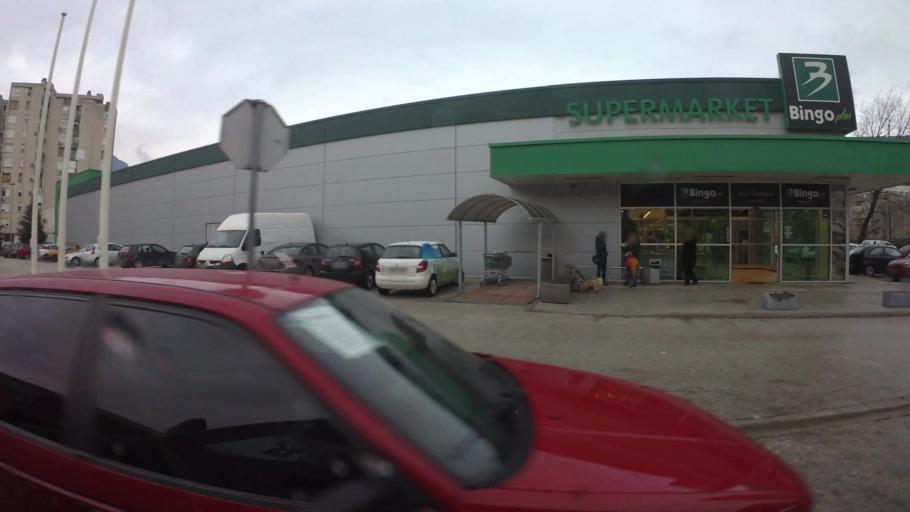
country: BA
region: Federation of Bosnia and Herzegovina
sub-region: Hercegovacko-Bosanski Kanton
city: Mostar
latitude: 43.3525
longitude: 17.8043
